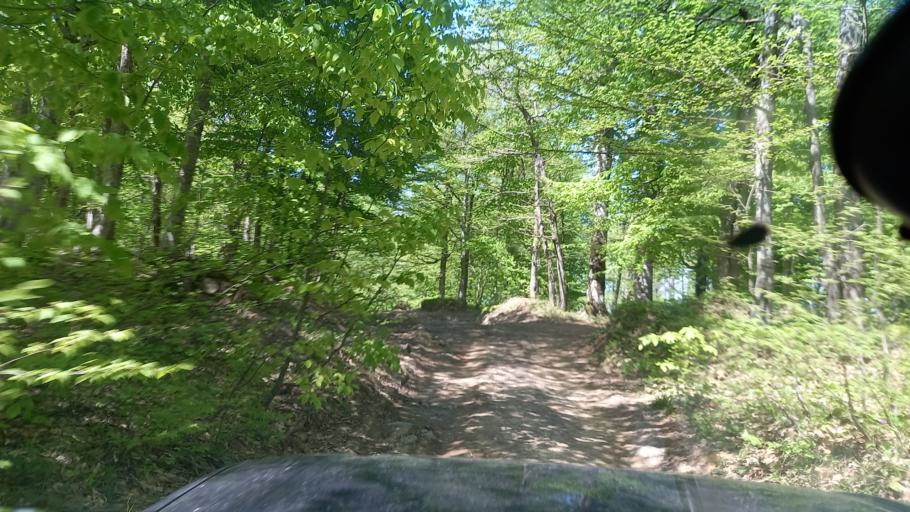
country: RU
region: Krasnodarskiy
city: Shepsi
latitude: 44.2473
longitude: 39.2986
